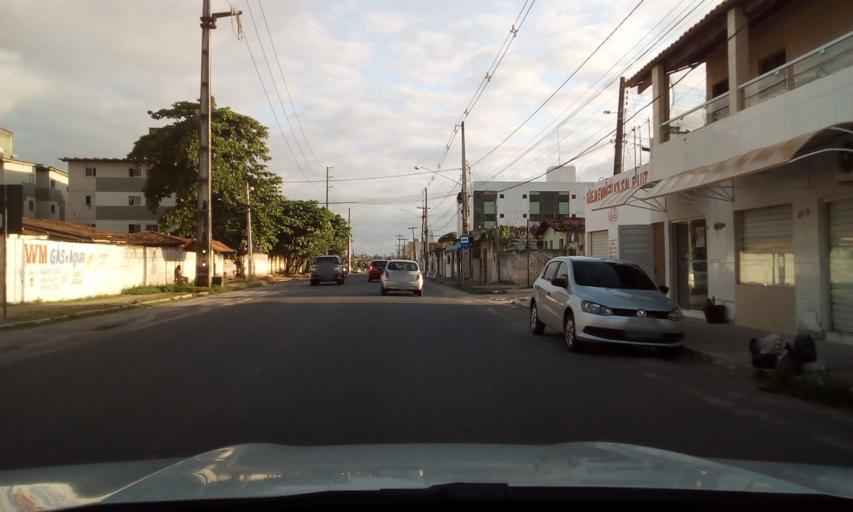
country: BR
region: Paraiba
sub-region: Joao Pessoa
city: Joao Pessoa
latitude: -7.1834
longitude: -34.8737
